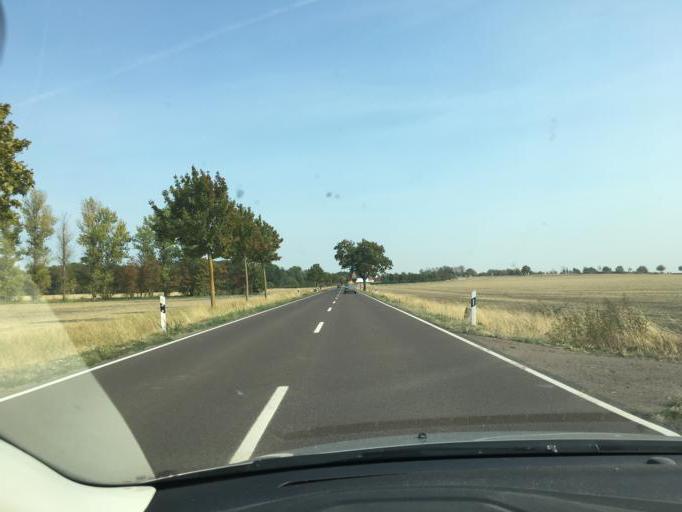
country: DE
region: Saxony-Anhalt
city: Wulfen
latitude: 51.7785
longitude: 11.8984
